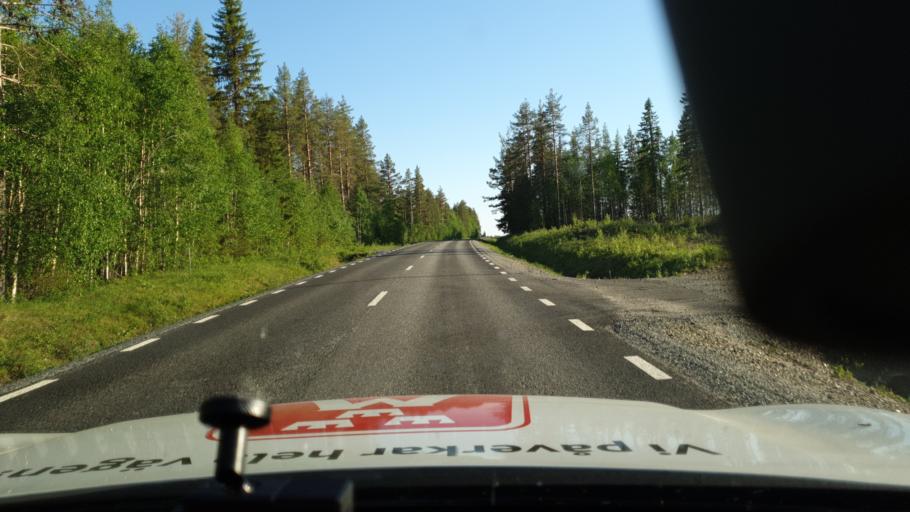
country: SE
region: Vaesterbotten
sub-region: Lycksele Kommun
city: Lycksele
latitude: 64.3930
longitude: 18.6047
